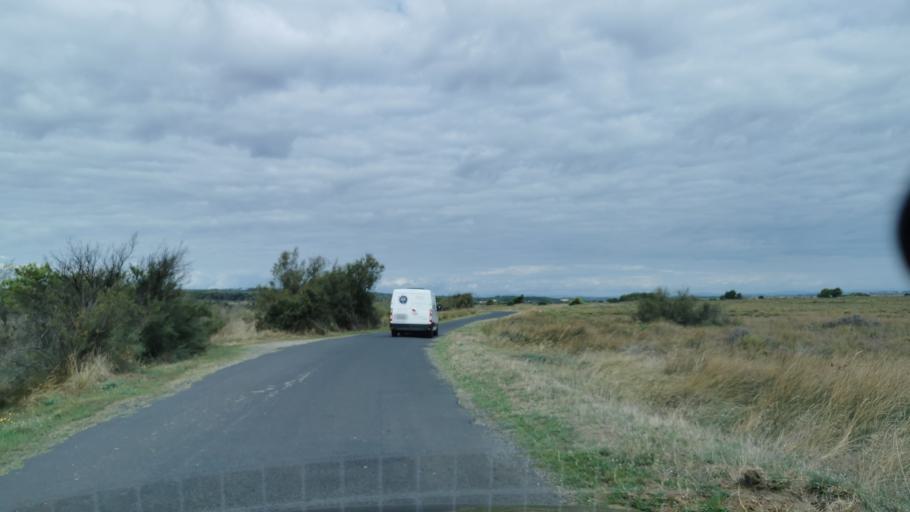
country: FR
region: Languedoc-Roussillon
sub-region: Departement de l'Aude
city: Fleury
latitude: 43.1948
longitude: 3.1977
